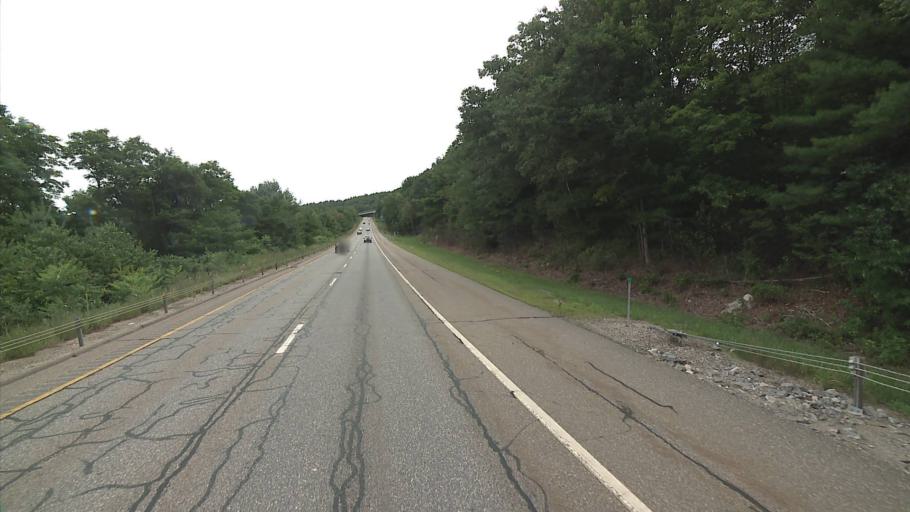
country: US
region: Connecticut
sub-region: Litchfield County
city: Torrington
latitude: 41.7807
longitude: -73.1110
